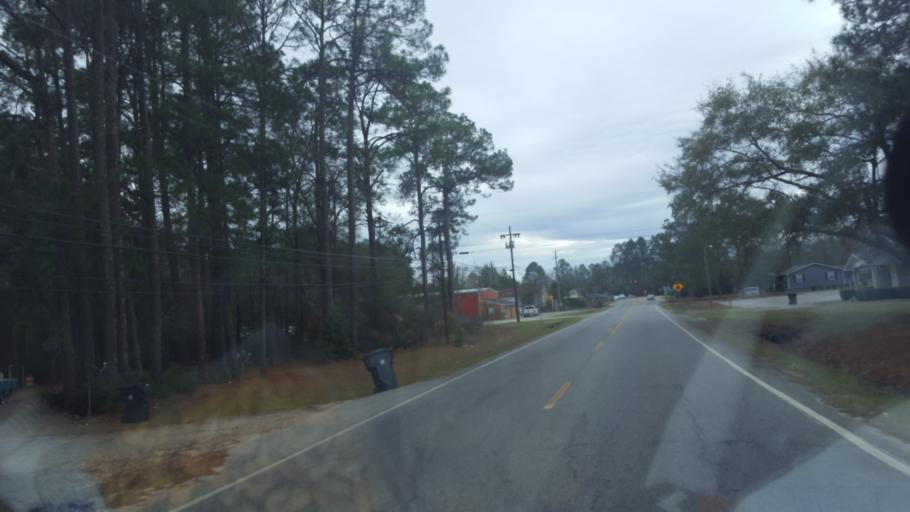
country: US
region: Georgia
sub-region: Ben Hill County
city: Fitzgerald
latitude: 31.7261
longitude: -83.2608
